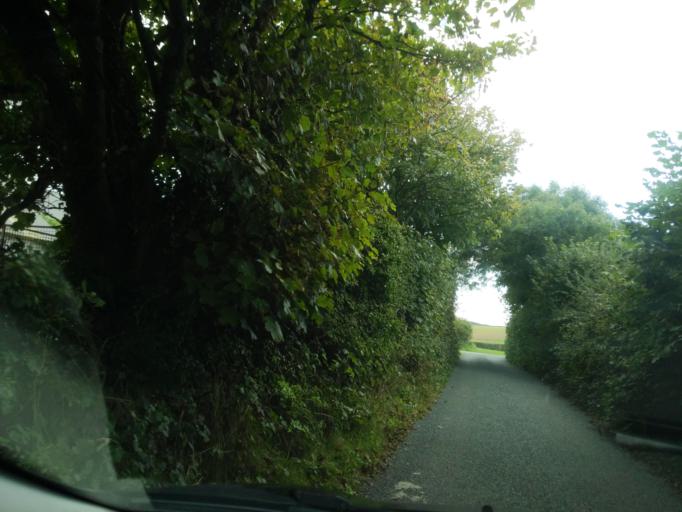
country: GB
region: England
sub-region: Plymouth
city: Plymstock
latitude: 50.3465
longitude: -4.1049
